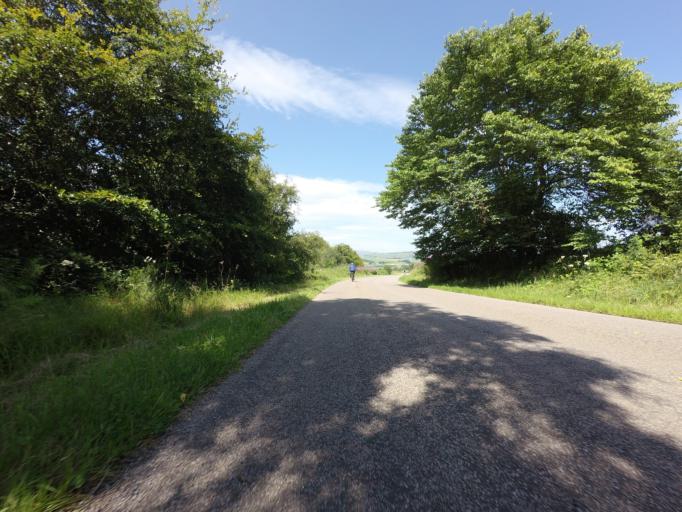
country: GB
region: Scotland
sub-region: Highland
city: Conon Bridge
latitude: 57.5651
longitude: -4.4221
